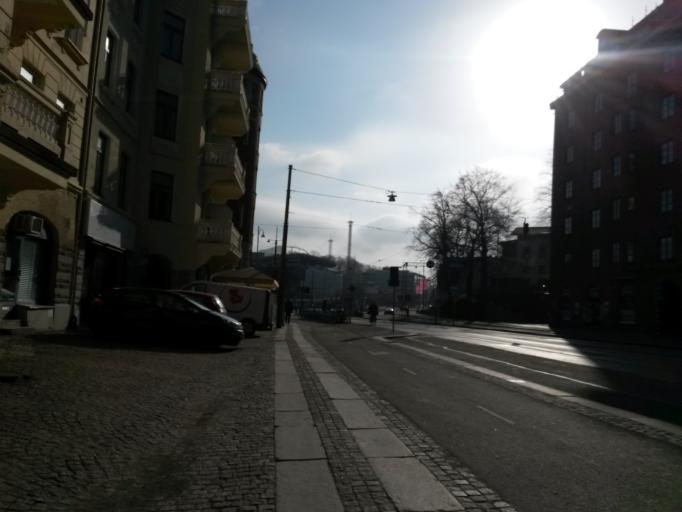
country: SE
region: Vaestra Goetaland
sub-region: Goteborg
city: Goeteborg
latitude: 57.6972
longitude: 11.9851
